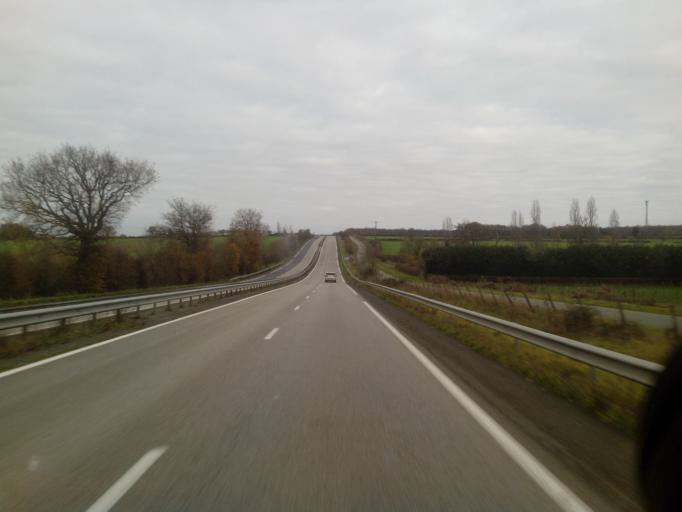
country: FR
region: Poitou-Charentes
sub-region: Departement des Deux-Sevres
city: La Peyratte
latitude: 46.6524
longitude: -0.1221
